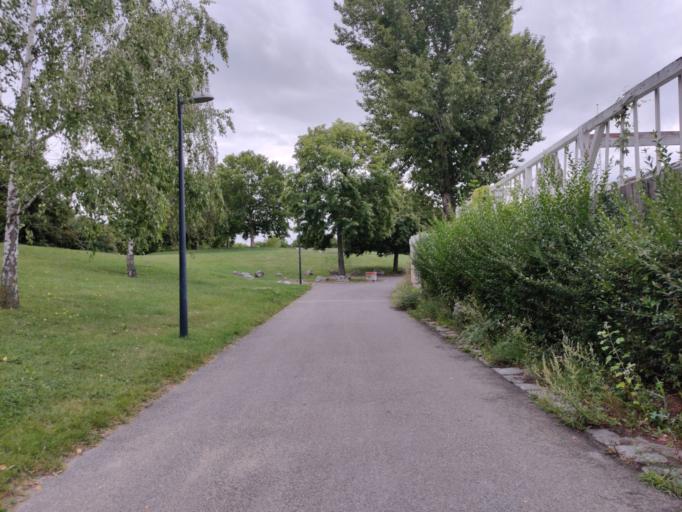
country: AT
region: Vienna
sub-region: Wien Stadt
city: Vienna
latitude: 48.2306
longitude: 16.4062
